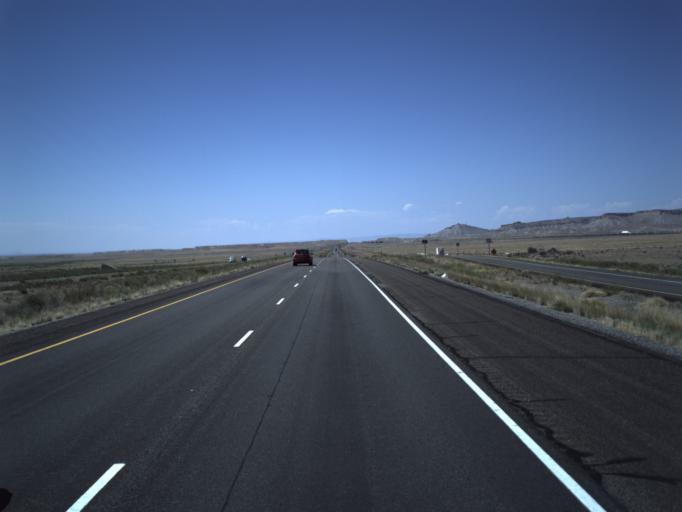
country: US
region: Utah
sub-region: Grand County
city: Moab
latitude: 38.9564
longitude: -109.7496
